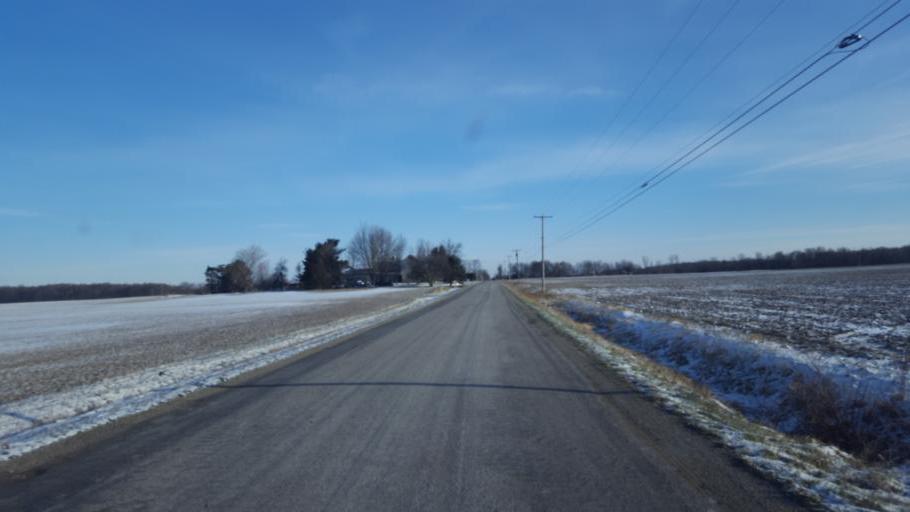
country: US
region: Ohio
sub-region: Morrow County
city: Mount Gilead
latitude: 40.6064
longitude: -82.8608
